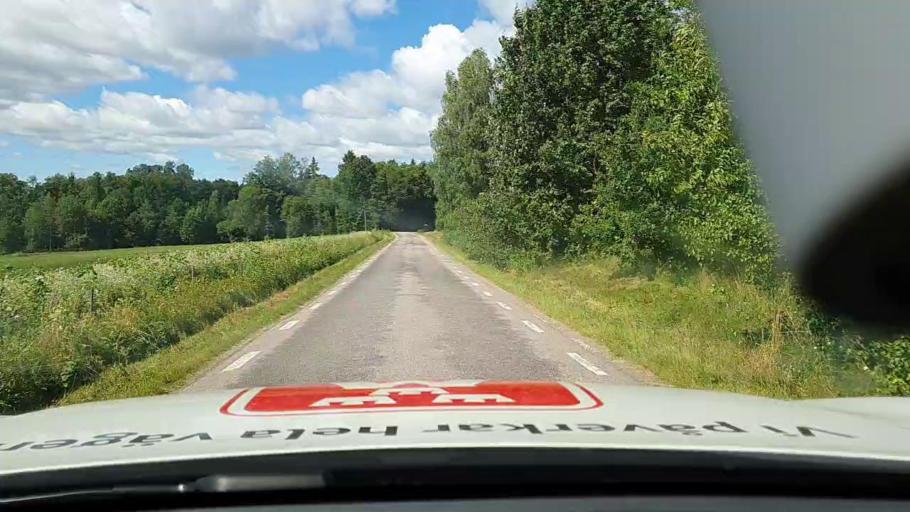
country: SE
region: Vaestra Goetaland
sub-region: Karlsborgs Kommun
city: Molltorp
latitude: 58.5898
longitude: 14.2666
